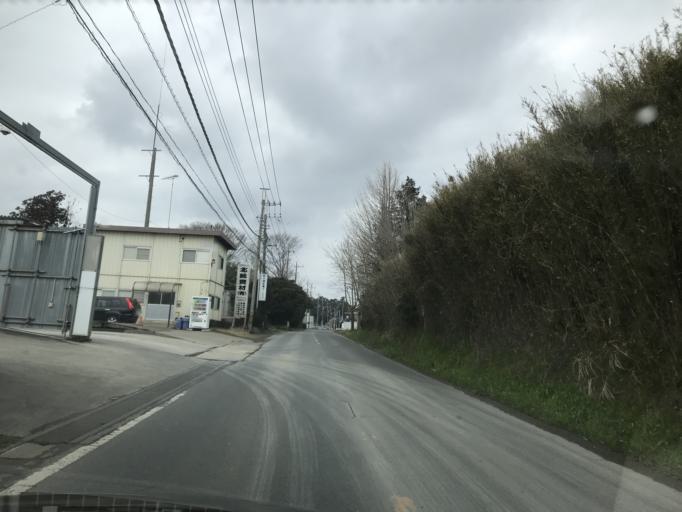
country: JP
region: Chiba
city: Sawara
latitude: 35.8418
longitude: 140.5061
